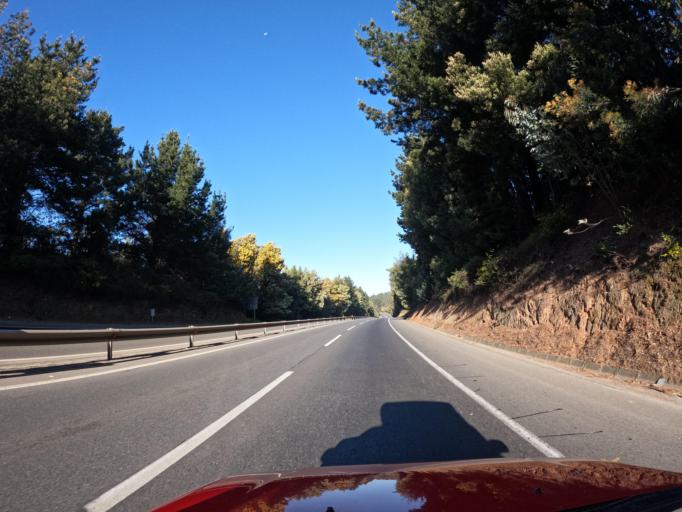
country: CL
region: Biobio
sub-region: Provincia de Concepcion
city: Penco
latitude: -36.7605
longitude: -72.9634
